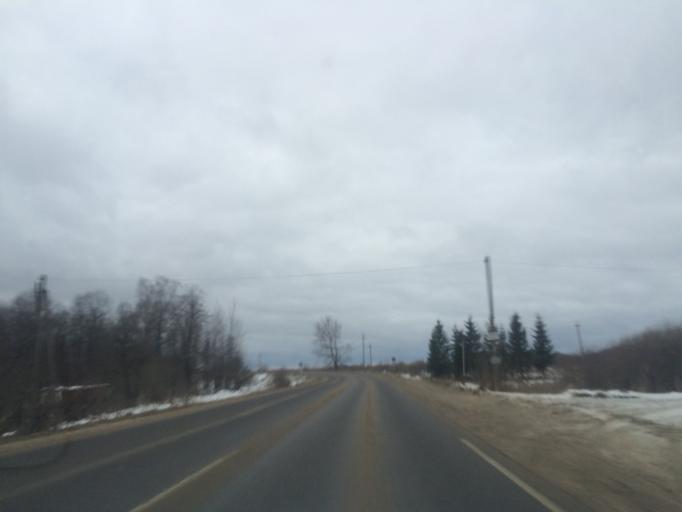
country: RU
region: Tula
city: Odoyev
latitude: 54.0077
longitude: 36.7764
